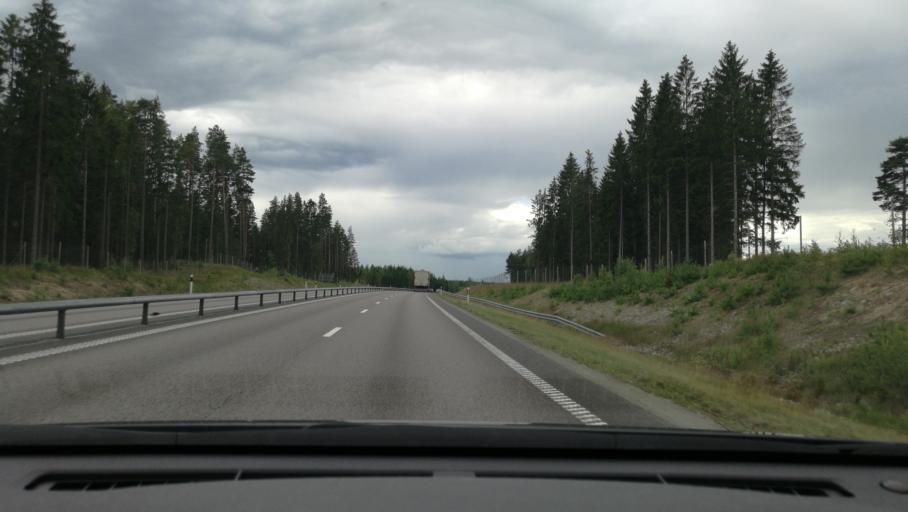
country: SE
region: Soedermanland
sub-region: Katrineholms Kommun
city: Katrineholm
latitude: 58.9669
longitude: 16.2541
